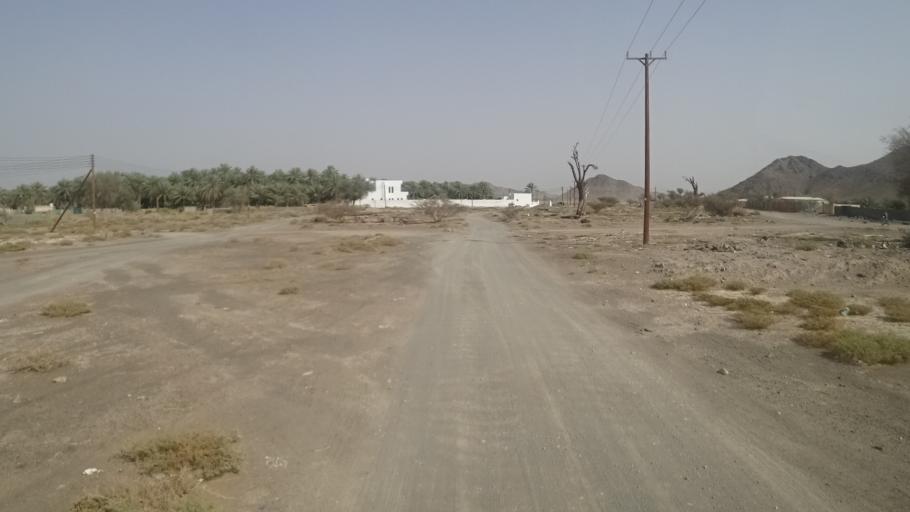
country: OM
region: Ash Sharqiyah
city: Ibra'
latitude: 22.7064
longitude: 58.1720
